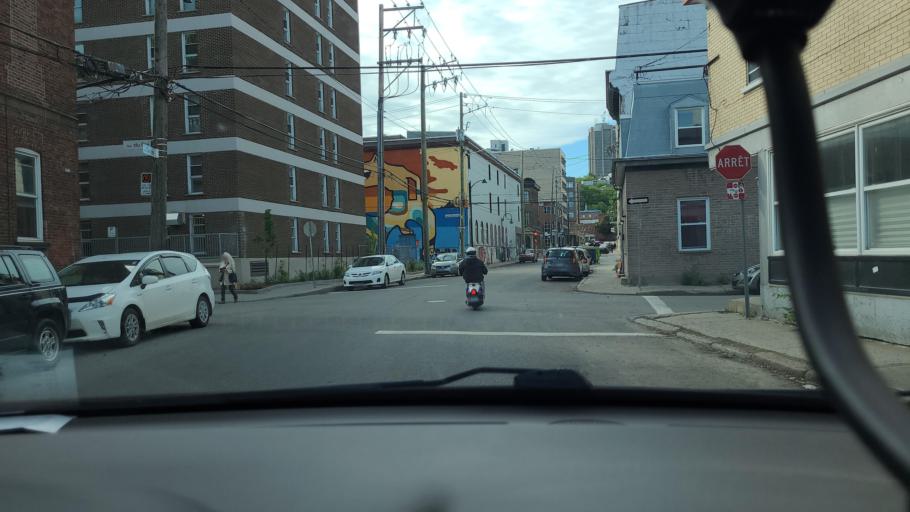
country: CA
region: Quebec
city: Quebec
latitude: 46.8138
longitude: -71.2291
